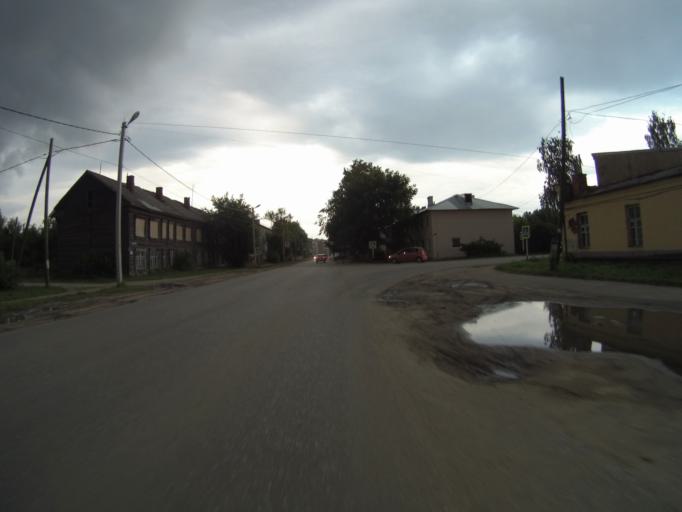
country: RU
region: Vladimir
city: Kameshkovo
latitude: 56.3476
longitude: 40.9882
